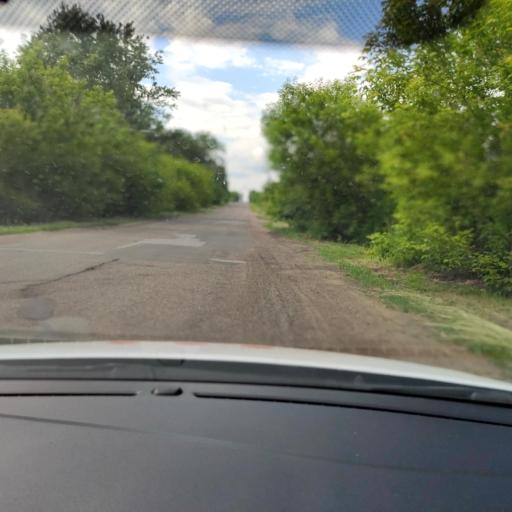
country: RU
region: Tatarstan
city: Stolbishchi
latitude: 55.7203
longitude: 49.2116
